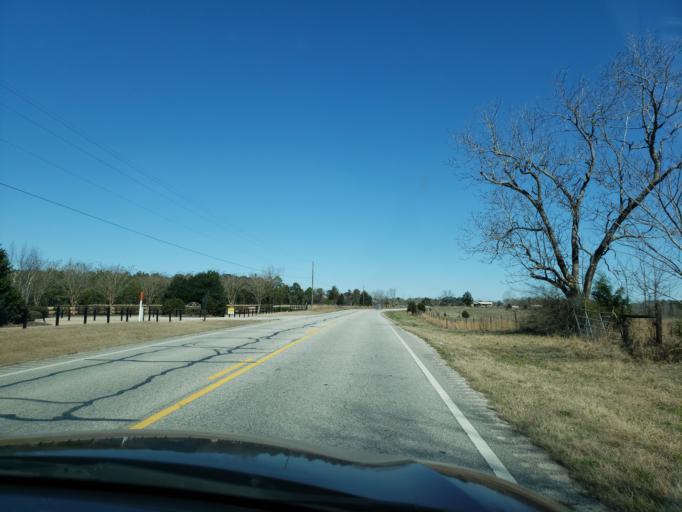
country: US
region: Alabama
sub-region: Macon County
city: Tuskegee
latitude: 32.5846
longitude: -85.6502
